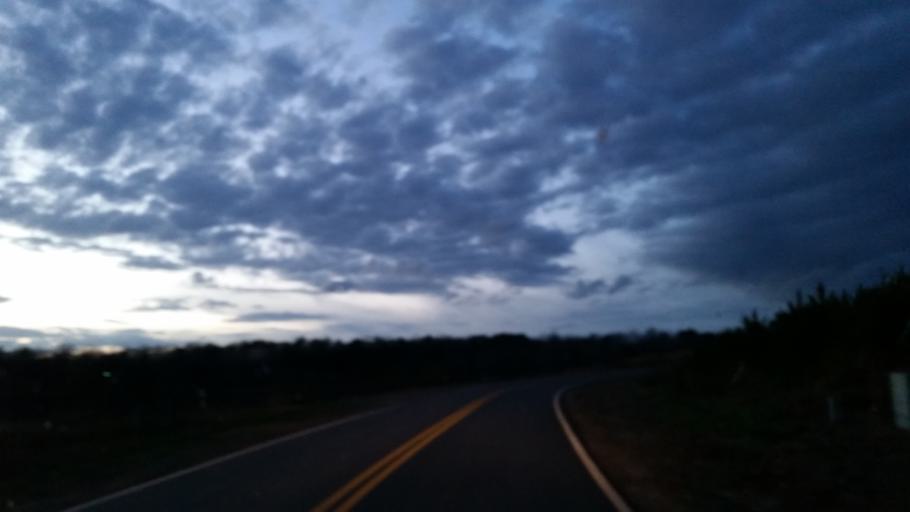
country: US
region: Georgia
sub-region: Cherokee County
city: Ball Ground
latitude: 34.3052
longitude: -84.4291
